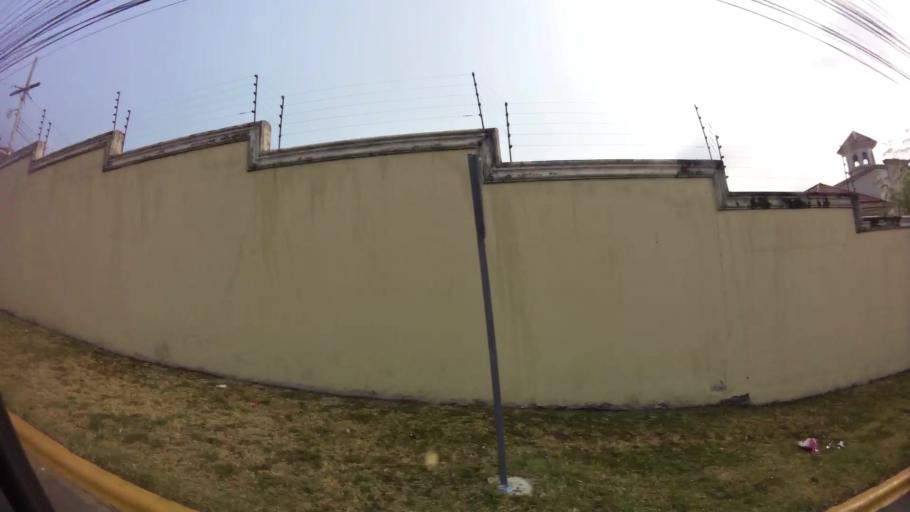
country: HN
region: Cortes
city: Armenta
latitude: 15.4980
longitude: -88.0484
